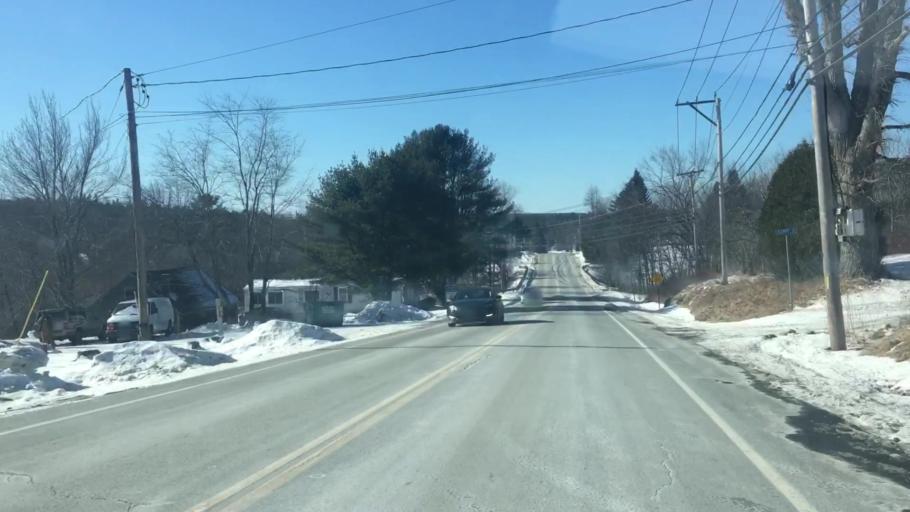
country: US
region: Maine
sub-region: Hancock County
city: Surry
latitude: 44.4957
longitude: -68.4992
